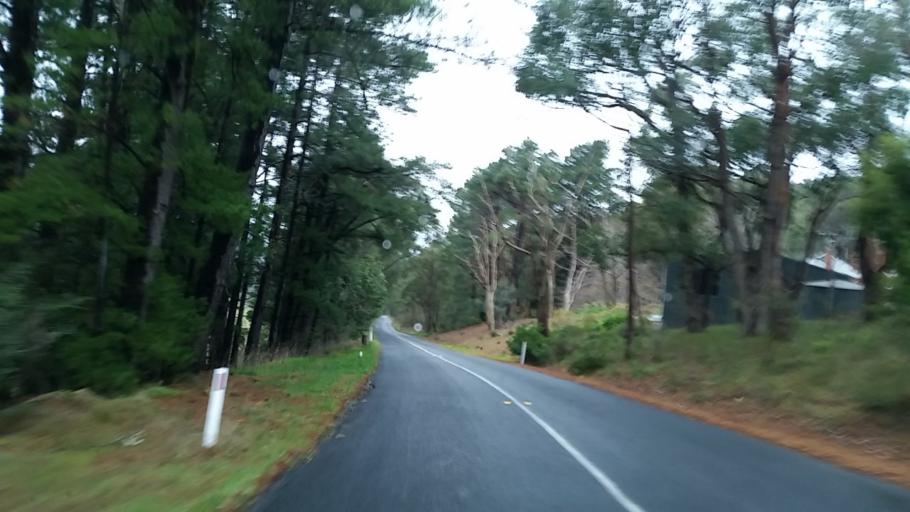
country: AU
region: South Australia
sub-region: Adelaide Hills
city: Bridgewater
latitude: -34.9515
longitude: 138.7610
